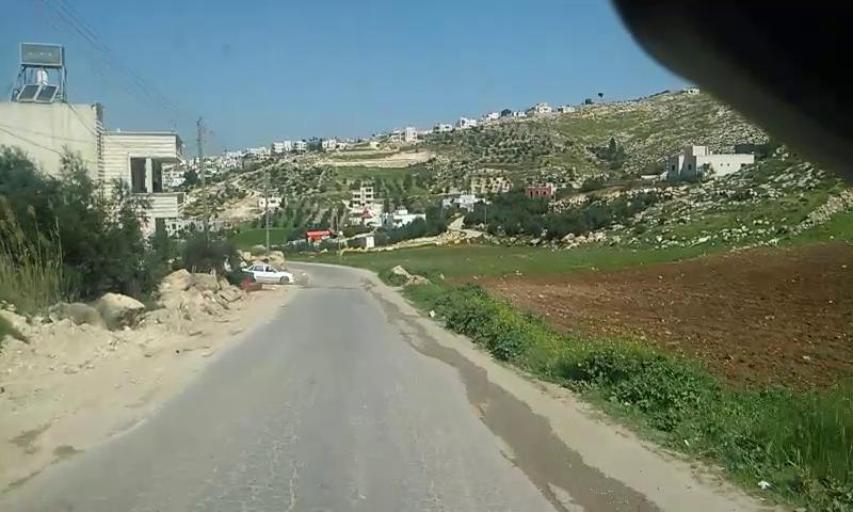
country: PS
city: Dayr Samit
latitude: 31.5061
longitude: 34.9691
